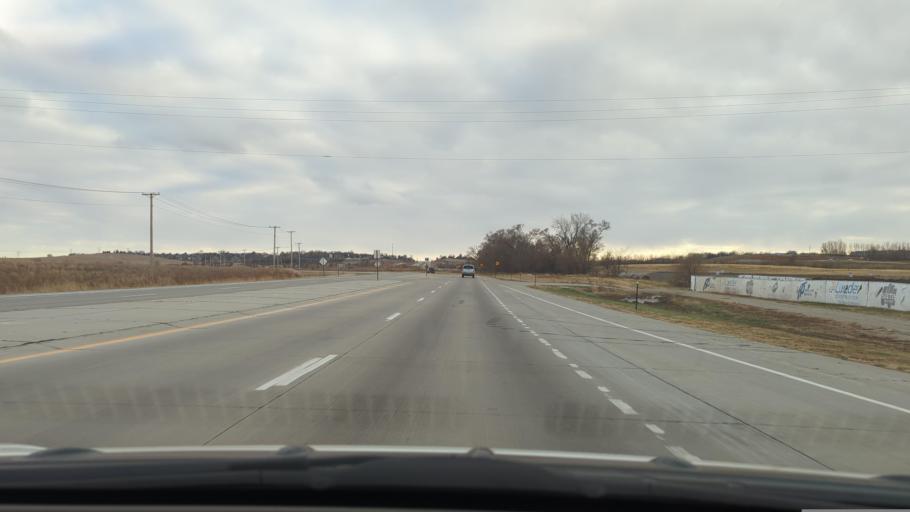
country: US
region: Nebraska
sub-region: Sarpy County
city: Offutt Air Force Base
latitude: 41.1101
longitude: -95.9282
